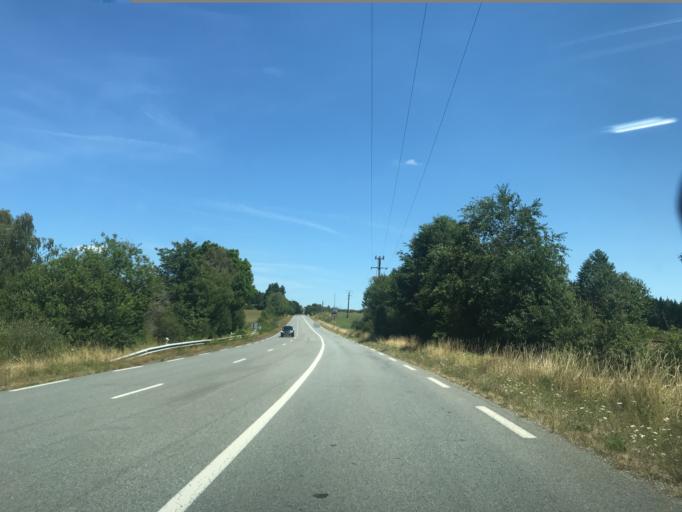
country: FR
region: Limousin
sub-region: Departement de la Correze
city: Correze
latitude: 45.3351
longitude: 1.9203
